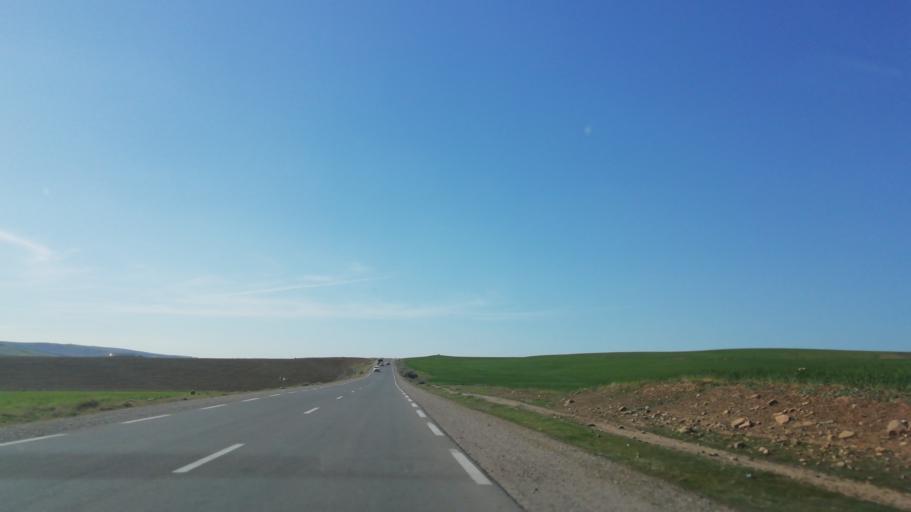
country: DZ
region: Mascara
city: Oued el Abtal
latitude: 35.4464
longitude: 0.8197
